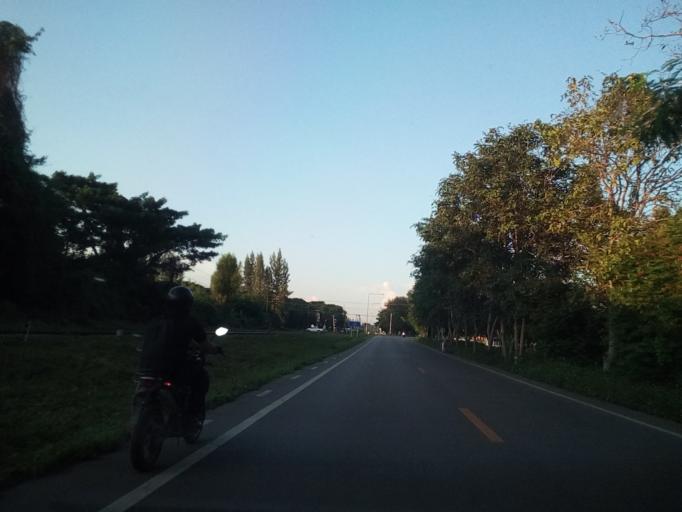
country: TH
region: Lamphun
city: Lamphun
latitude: 18.6347
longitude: 99.0415
